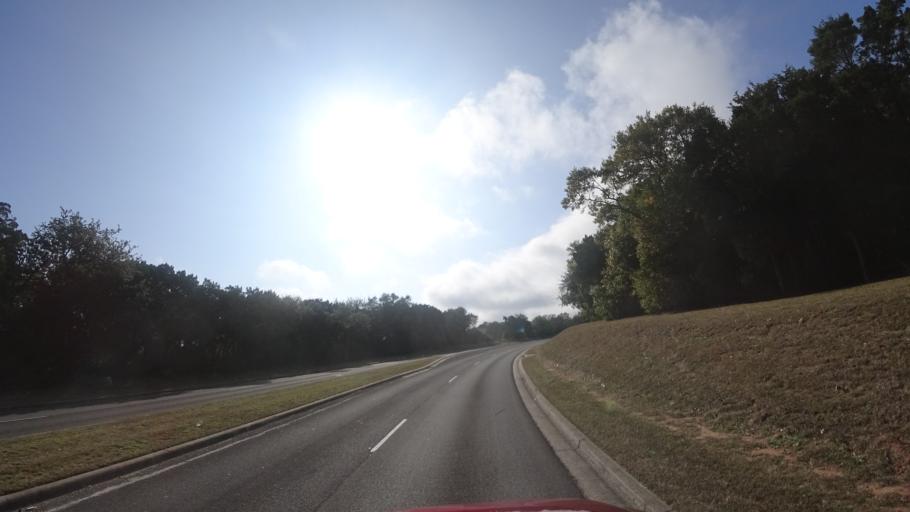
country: US
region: Texas
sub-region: Williamson County
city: Anderson Mill
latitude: 30.4032
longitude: -97.8463
